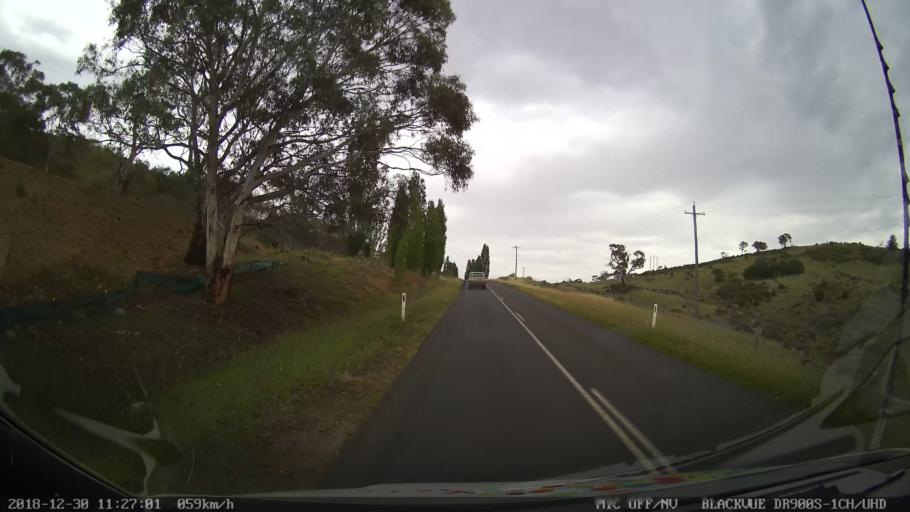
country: AU
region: New South Wales
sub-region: Snowy River
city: Jindabyne
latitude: -36.4637
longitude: 148.6295
